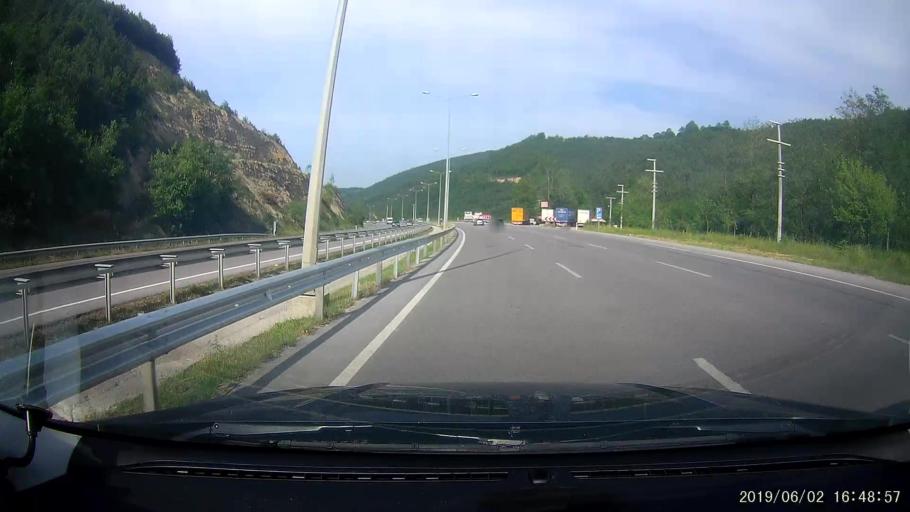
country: TR
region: Samsun
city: Taflan
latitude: 41.2319
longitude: 36.1504
